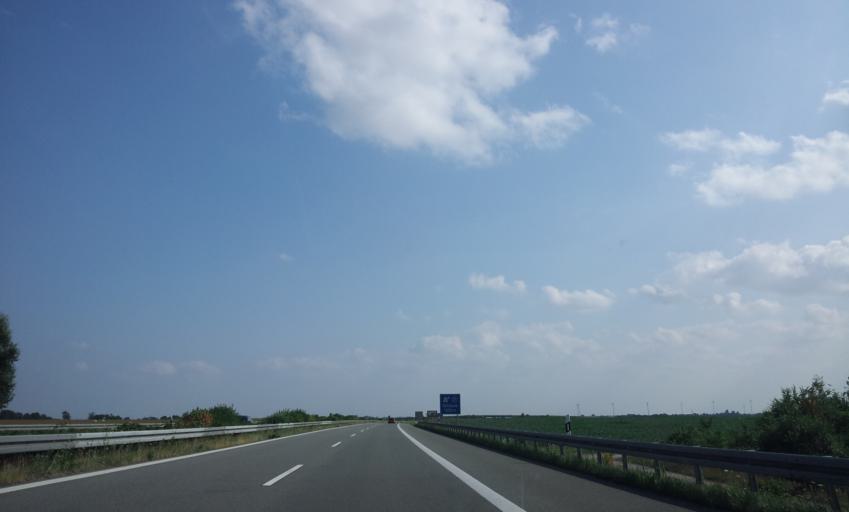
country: DE
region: Mecklenburg-Vorpommern
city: Jarmen
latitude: 53.9592
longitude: 13.3679
